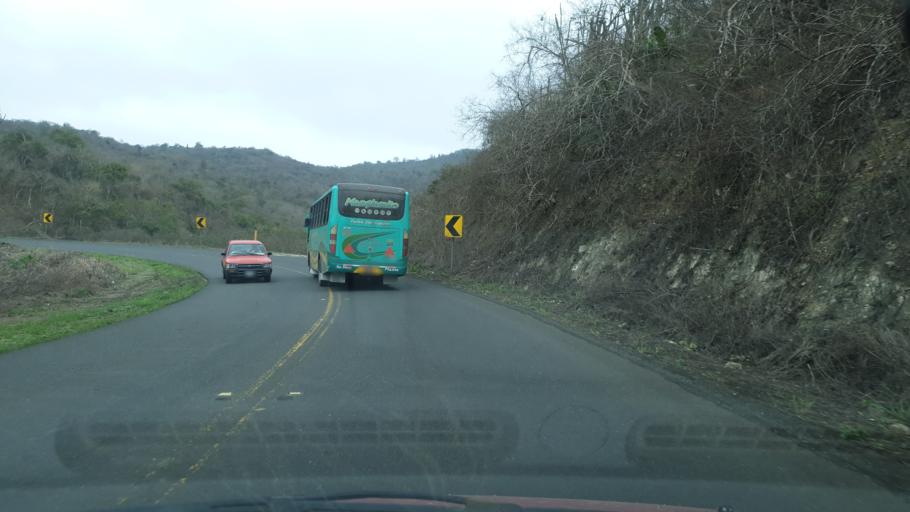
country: EC
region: Manabi
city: Jipijapa
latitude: -1.3689
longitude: -80.7330
